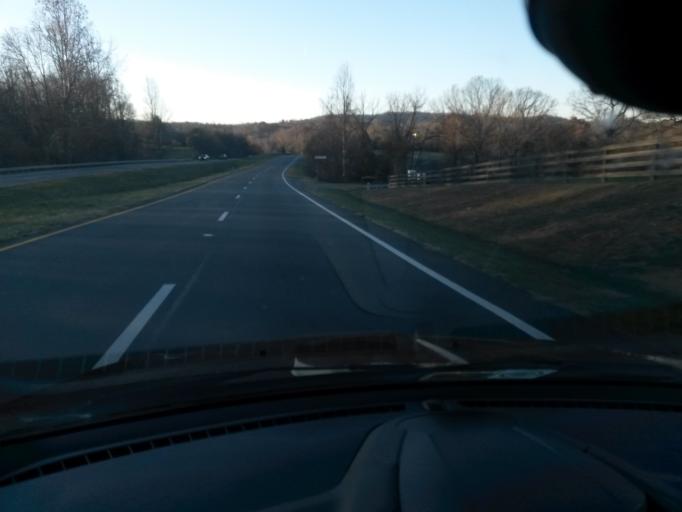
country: US
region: Virginia
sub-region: Franklin County
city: Henry Fork
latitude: 36.9372
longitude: -79.8738
